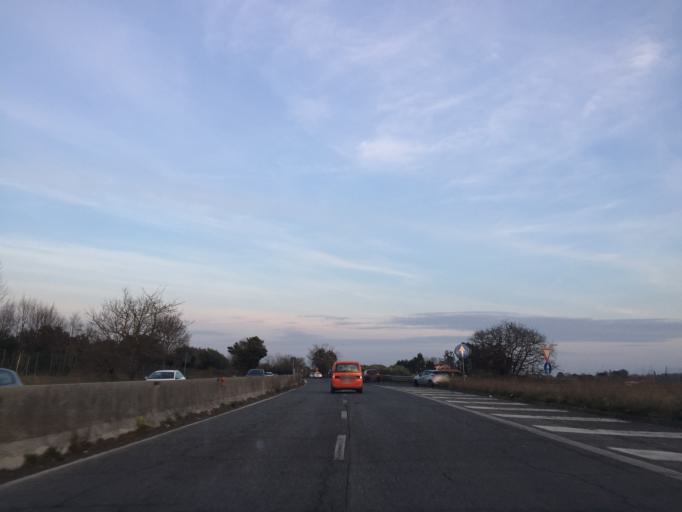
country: IT
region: Latium
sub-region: Citta metropolitana di Roma Capitale
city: Formello
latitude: 42.0453
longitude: 12.3957
